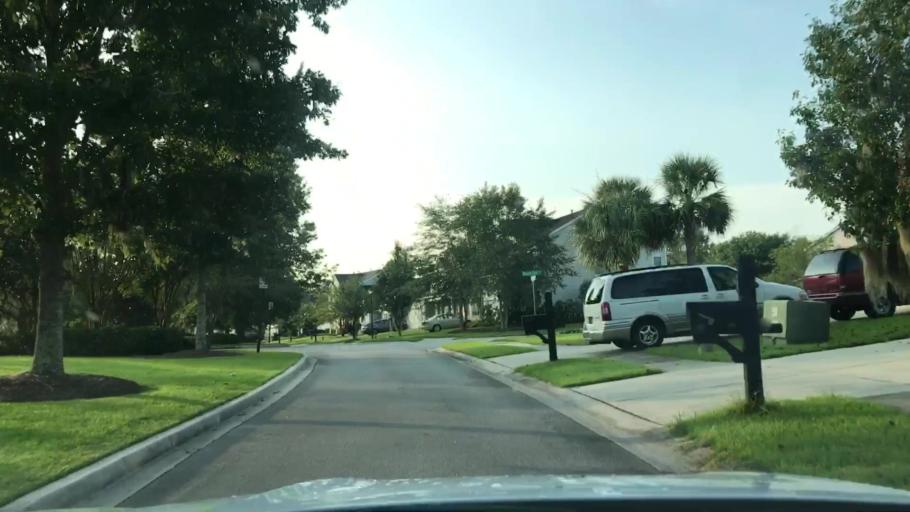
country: US
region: South Carolina
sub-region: Charleston County
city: Shell Point
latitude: 32.8357
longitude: -80.0924
